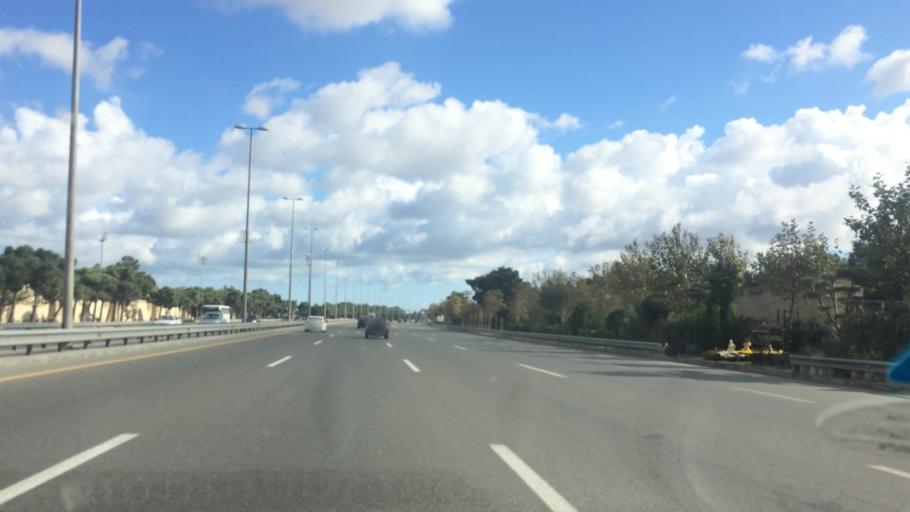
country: AZ
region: Baki
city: Biny Selo
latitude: 40.4617
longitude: 50.0800
